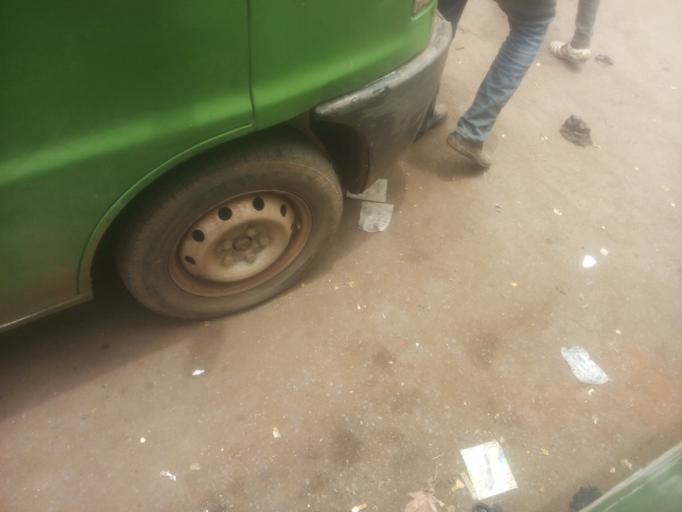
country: ML
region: Bamako
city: Bamako
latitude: 12.6502
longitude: -7.9934
